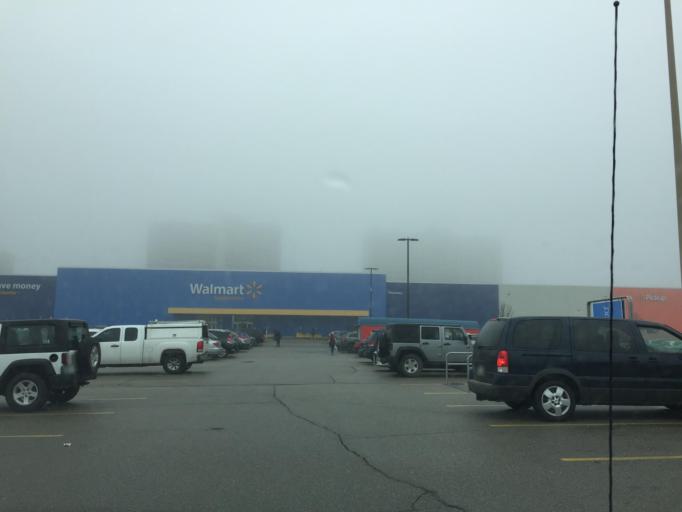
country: CA
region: Ontario
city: Kitchener
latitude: 43.4249
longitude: -80.4366
